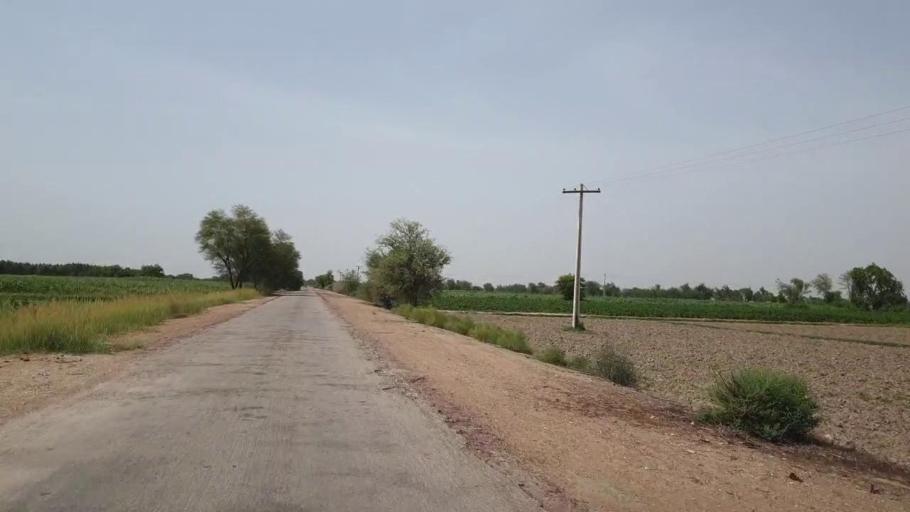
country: PK
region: Sindh
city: Daur
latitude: 26.5297
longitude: 68.4075
